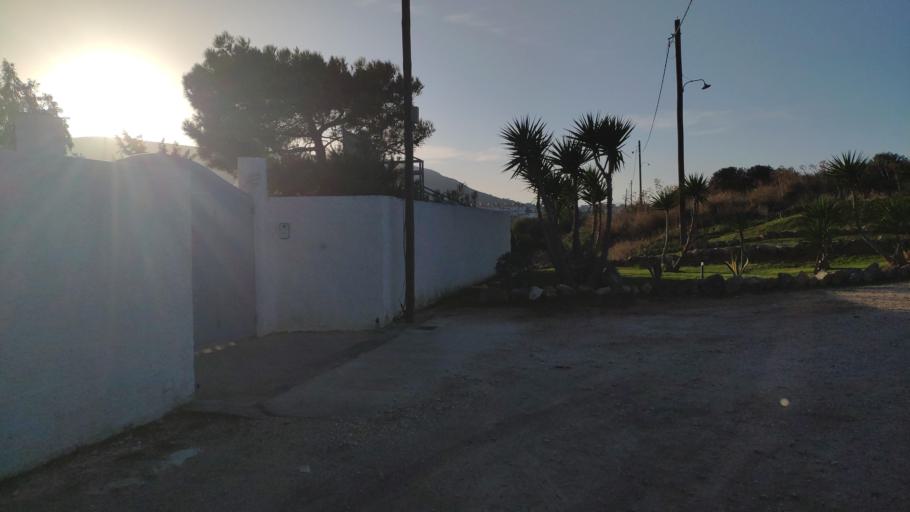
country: GR
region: Attica
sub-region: Nomarchia Anatolikis Attikis
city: Limin Mesoyaias
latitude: 37.8849
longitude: 24.0178
